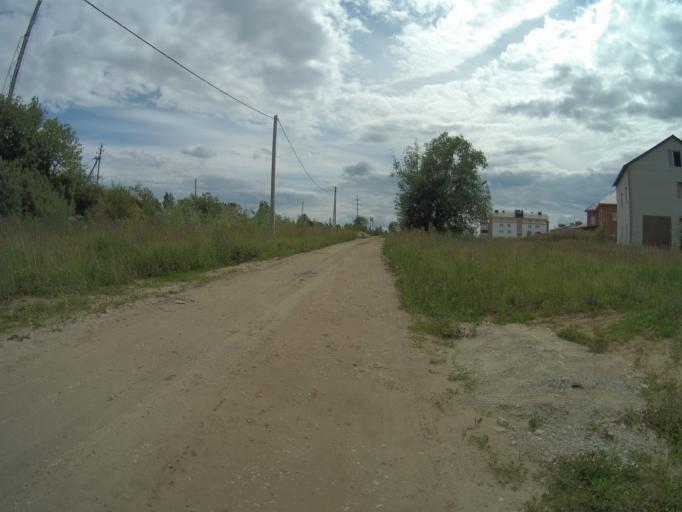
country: RU
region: Vladimir
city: Bogolyubovo
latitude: 56.2011
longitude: 40.5266
